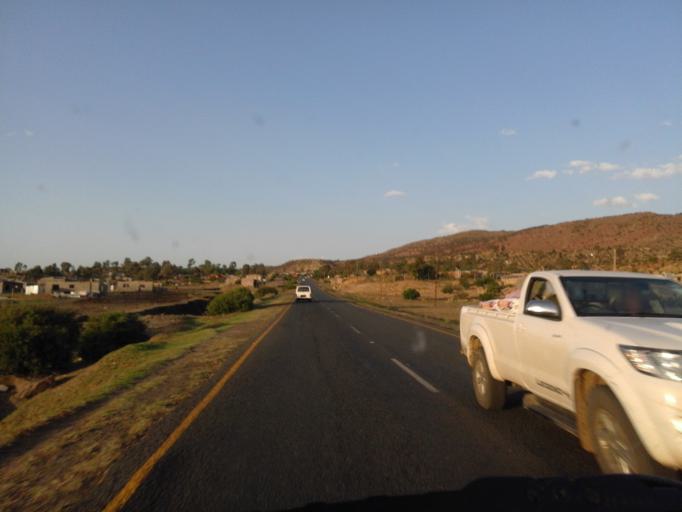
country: LS
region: Mafeteng
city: Mafeteng
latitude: -29.8448
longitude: 27.2297
